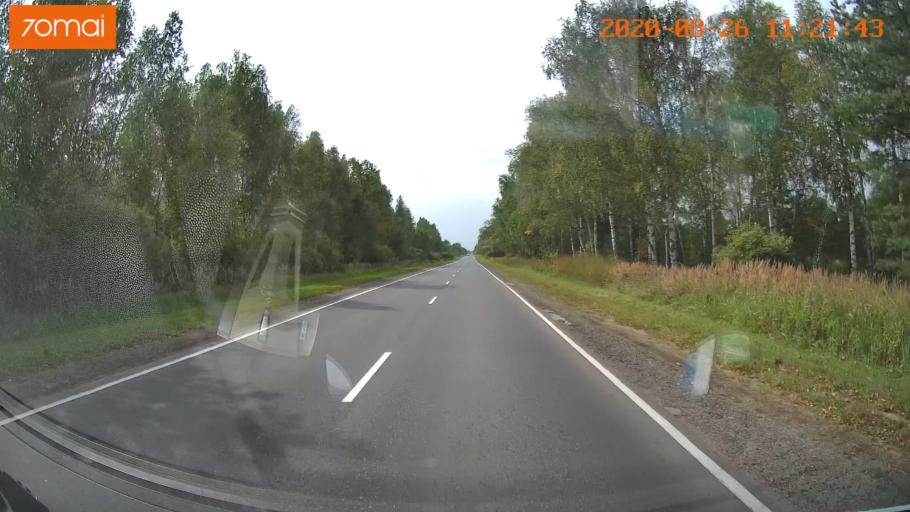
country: RU
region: Rjazan
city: Shilovo
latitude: 54.3729
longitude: 41.0400
